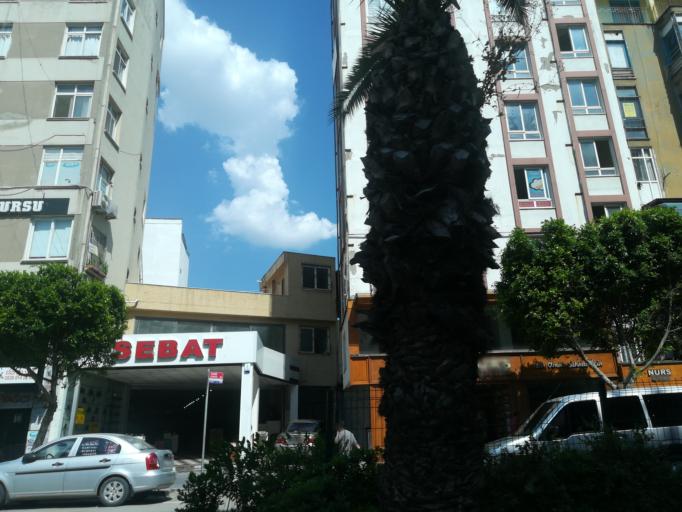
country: TR
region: Adana
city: Adana
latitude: 36.9895
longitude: 35.3233
